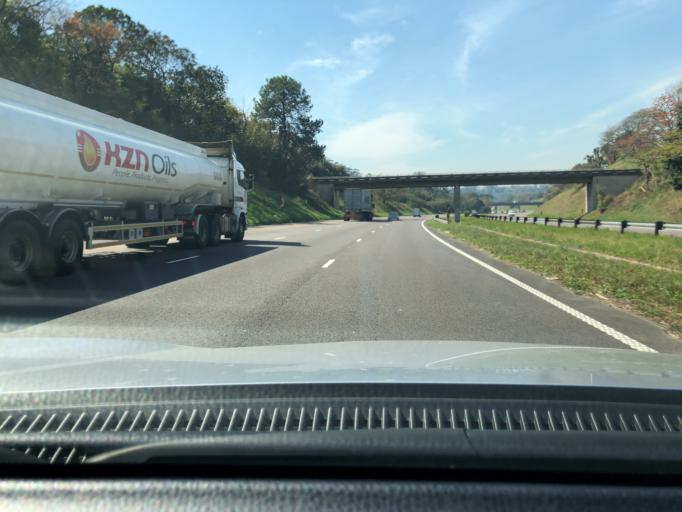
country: ZA
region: KwaZulu-Natal
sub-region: eThekwini Metropolitan Municipality
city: Berea
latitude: -29.8341
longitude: 30.8820
